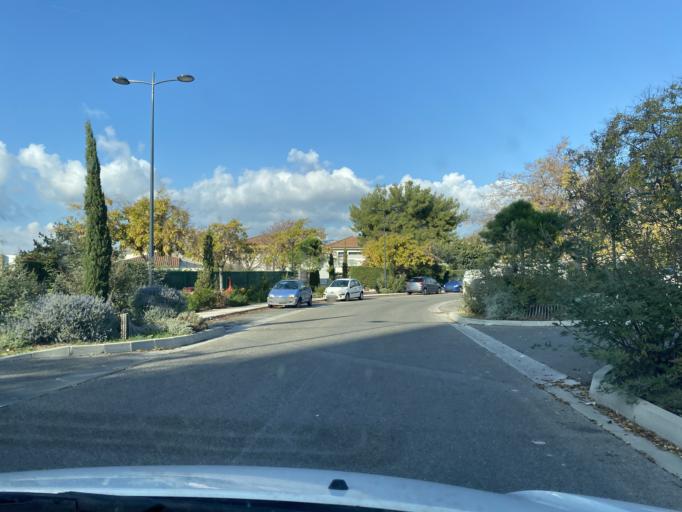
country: FR
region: Provence-Alpes-Cote d'Azur
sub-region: Departement du Var
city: La Seyne-sur-Mer
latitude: 43.1120
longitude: 5.8697
